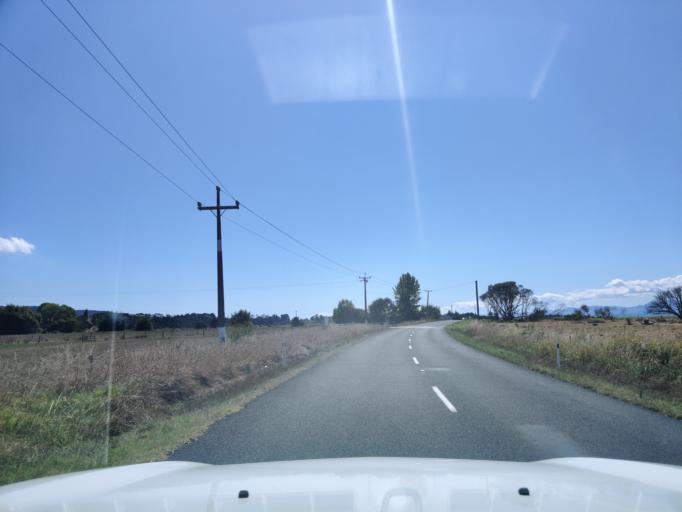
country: NZ
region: Waikato
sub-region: Thames-Coromandel District
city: Thames
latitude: -37.0690
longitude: 175.2958
